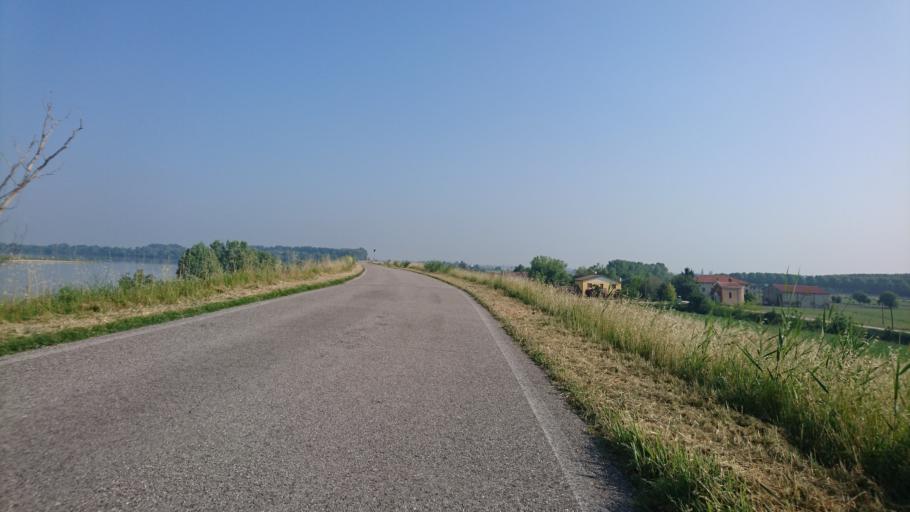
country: IT
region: Veneto
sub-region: Provincia di Rovigo
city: Castelnovo Bariano
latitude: 45.0469
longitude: 11.2733
